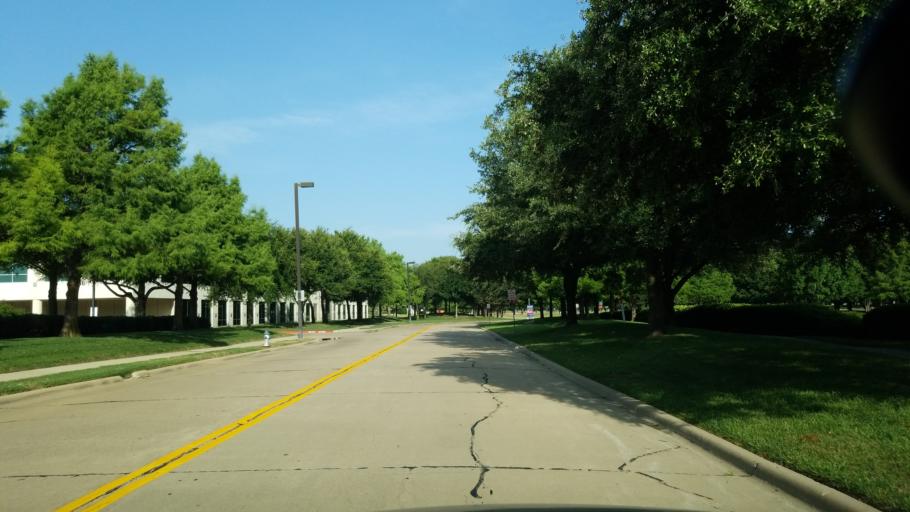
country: US
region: Texas
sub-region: Dallas County
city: Coppell
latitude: 32.9254
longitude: -97.0110
